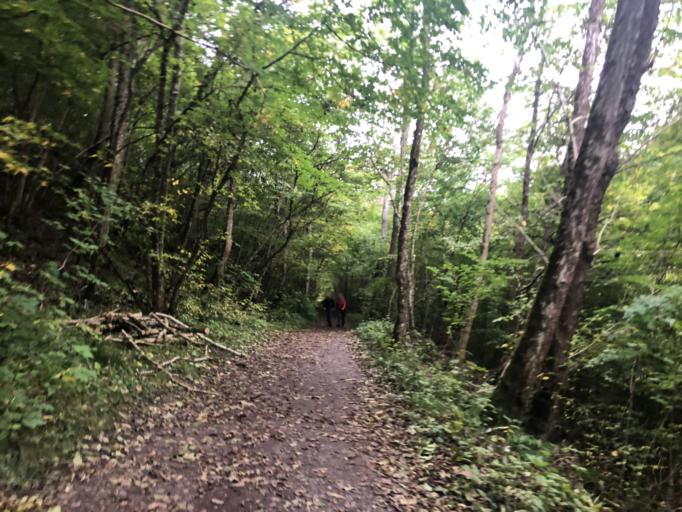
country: GB
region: Scotland
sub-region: Perth and Kinross
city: Pitlochry
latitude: 56.7320
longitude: -3.7742
